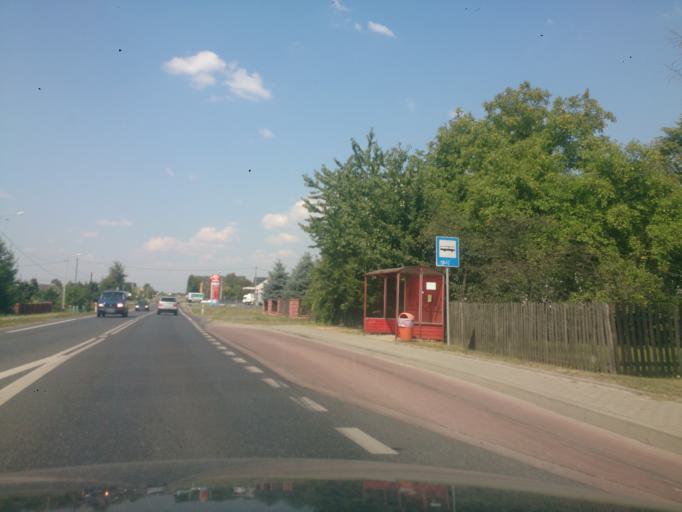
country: PL
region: Subcarpathian Voivodeship
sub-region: Powiat kolbuszowski
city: Kolbuszowa
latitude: 50.2568
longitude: 21.7677
